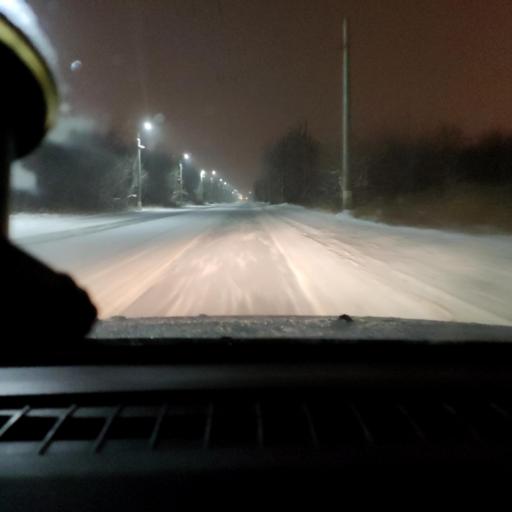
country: RU
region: Samara
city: Novokuybyshevsk
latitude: 53.0787
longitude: 49.9280
